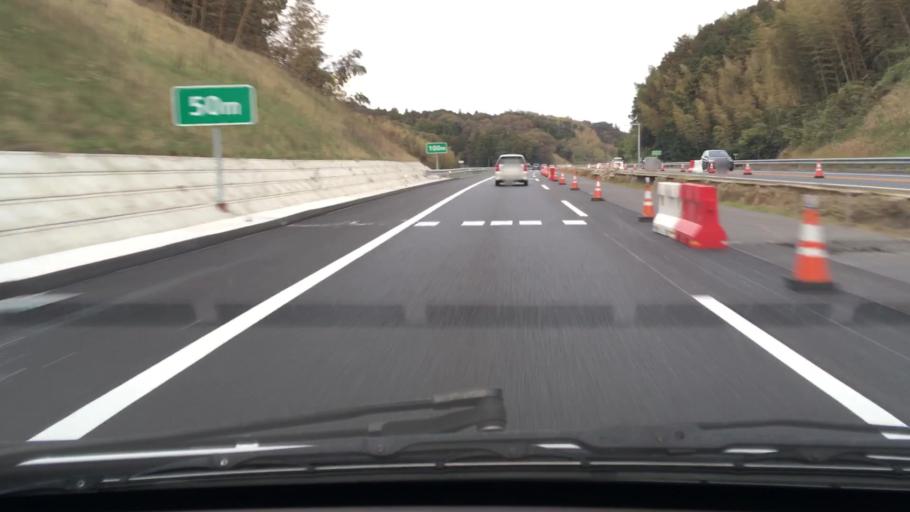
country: JP
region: Chiba
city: Kimitsu
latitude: 35.2925
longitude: 139.9311
